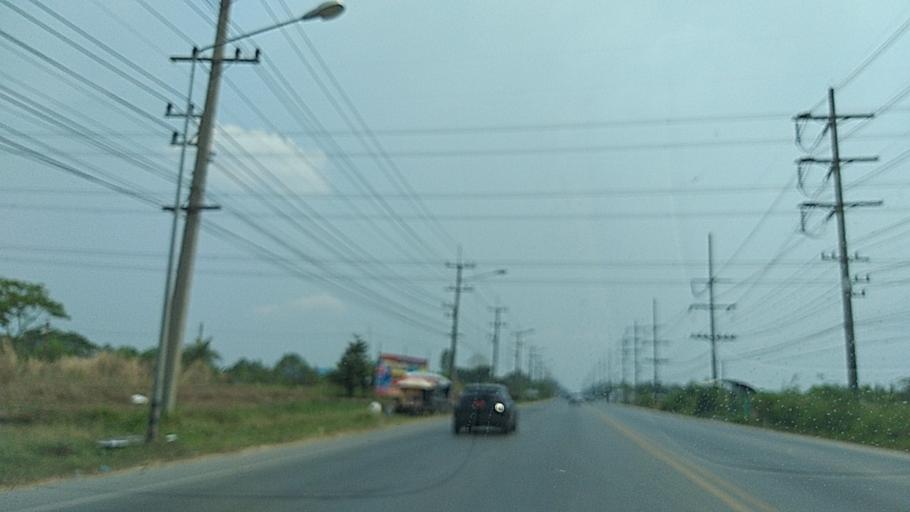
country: TH
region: Pathum Thani
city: Ban Lam Luk Ka
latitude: 13.9592
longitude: 100.8774
